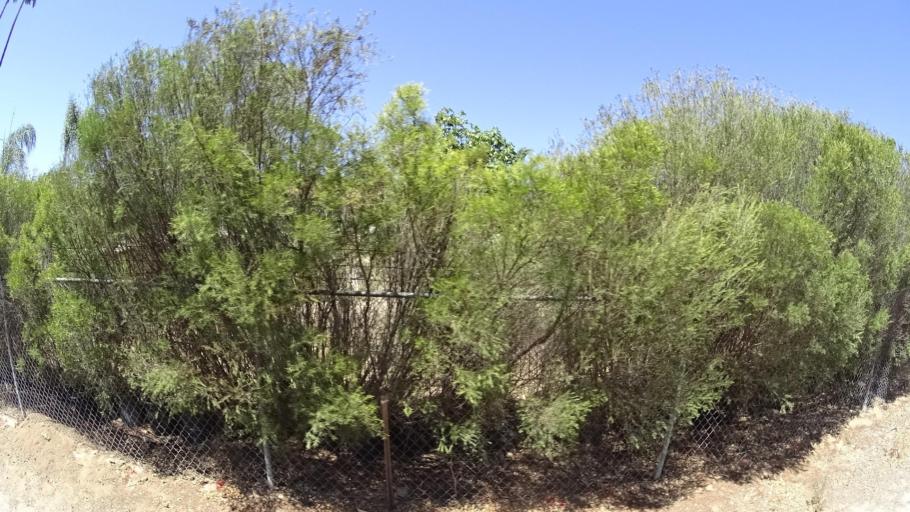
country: US
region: California
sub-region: San Diego County
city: Bonsall
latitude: 33.3325
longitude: -117.1729
